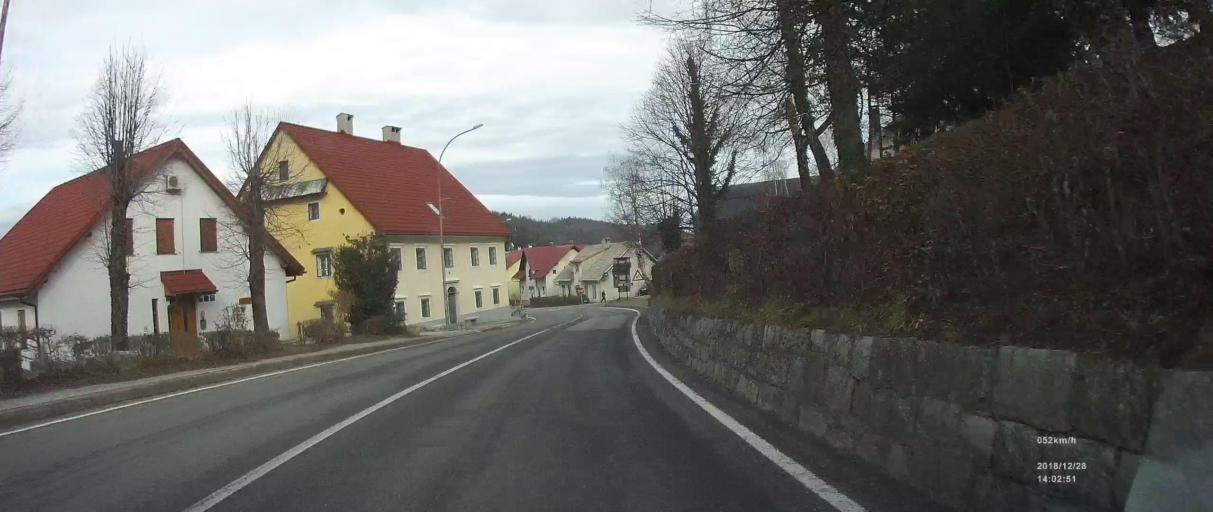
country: SI
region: Kostel
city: Kostel
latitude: 45.4321
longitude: 14.9048
